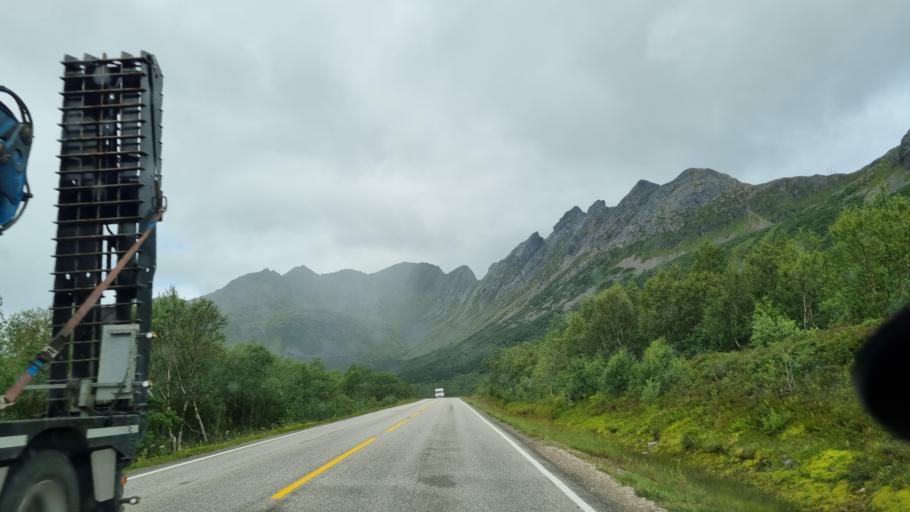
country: NO
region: Nordland
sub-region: Vagan
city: Kabelvag
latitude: 68.2137
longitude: 14.3336
